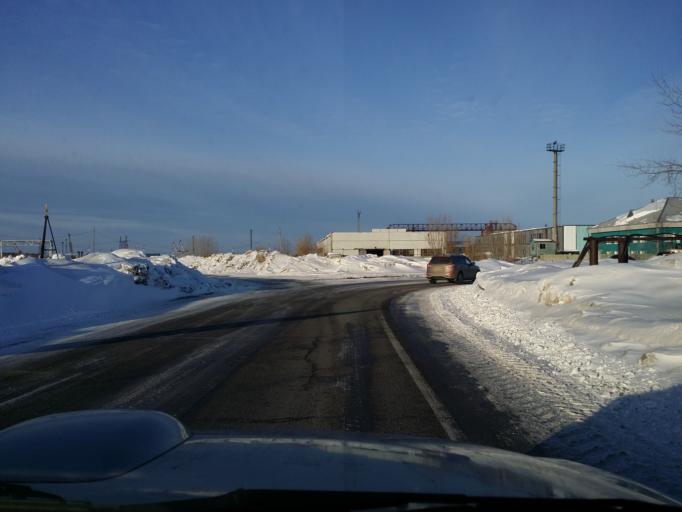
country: RU
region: Khanty-Mansiyskiy Avtonomnyy Okrug
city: Izluchinsk
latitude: 60.9822
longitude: 76.9061
